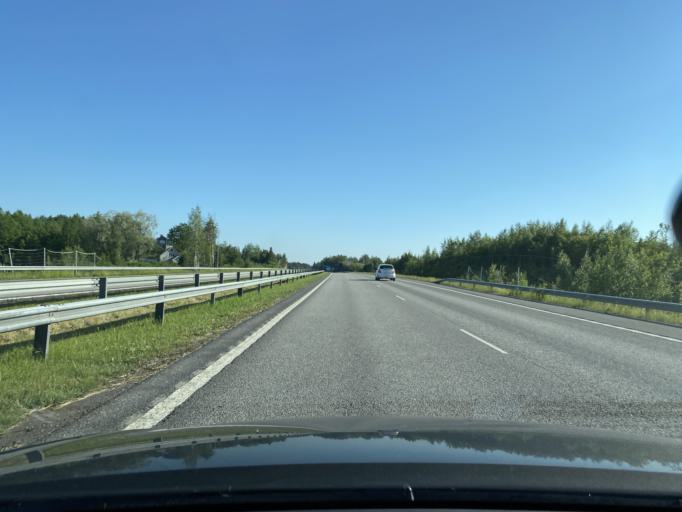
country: FI
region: Varsinais-Suomi
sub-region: Turku
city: Turku
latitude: 60.5178
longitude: 22.3031
